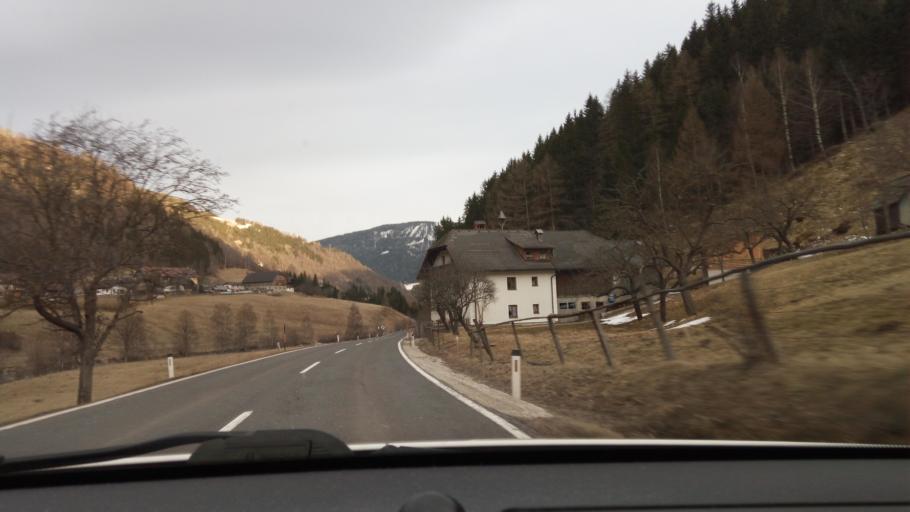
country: AT
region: Salzburg
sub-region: Politischer Bezirk Tamsweg
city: Ramingstein
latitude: 47.0733
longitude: 13.8585
